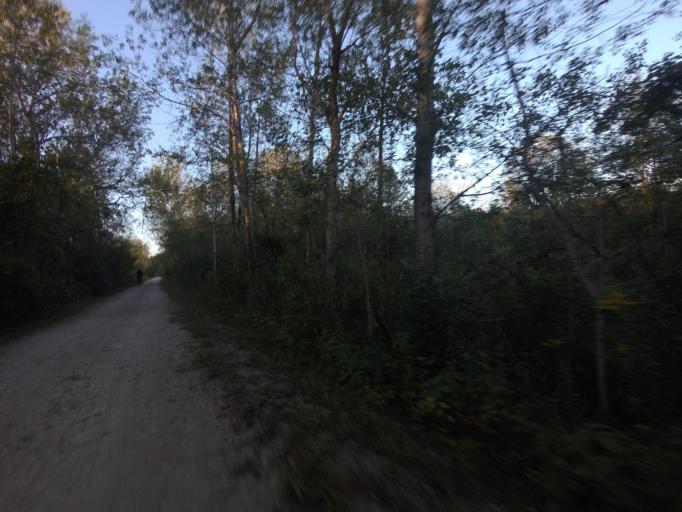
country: CA
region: Ontario
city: Brampton
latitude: 43.9072
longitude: -79.8385
